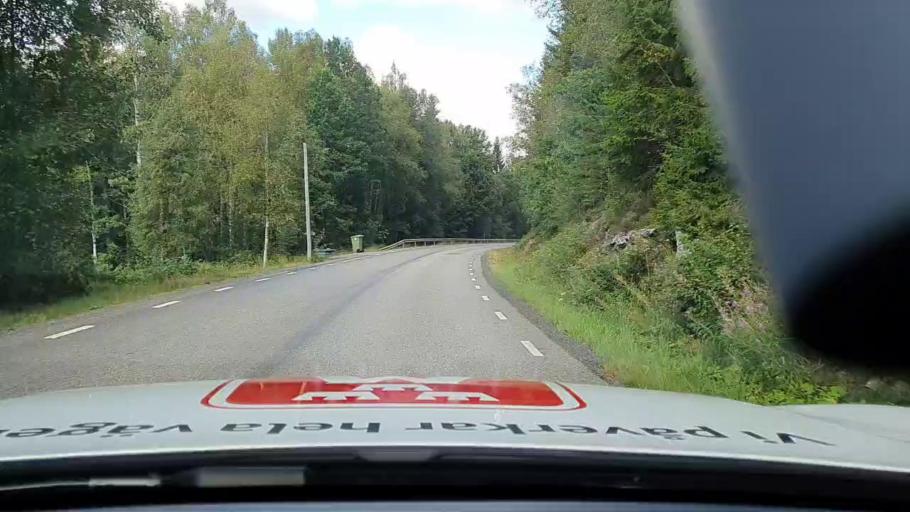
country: SE
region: Vaestra Goetaland
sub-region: Marks Kommun
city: Fritsla
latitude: 57.3999
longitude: 12.8506
